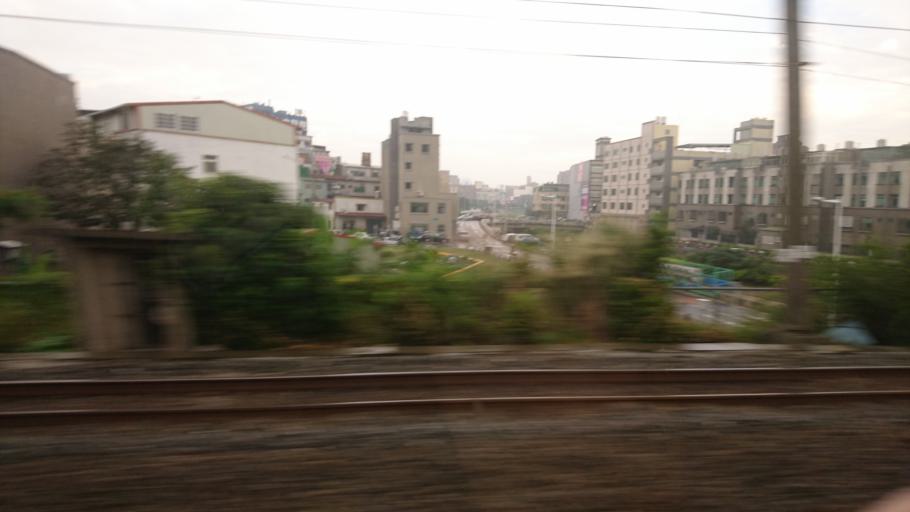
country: TW
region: Taiwan
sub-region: Hsinchu
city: Zhubei
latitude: 24.8354
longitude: 121.0064
